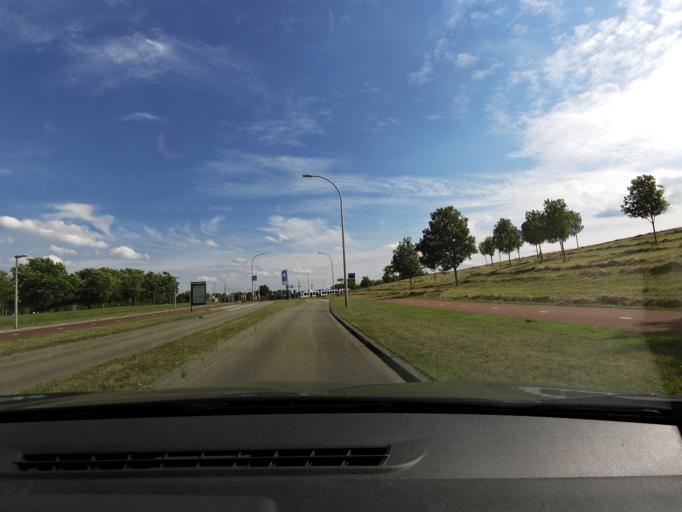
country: NL
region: South Holland
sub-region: Gemeente Den Haag
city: Ypenburg
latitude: 52.0328
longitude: 4.3556
